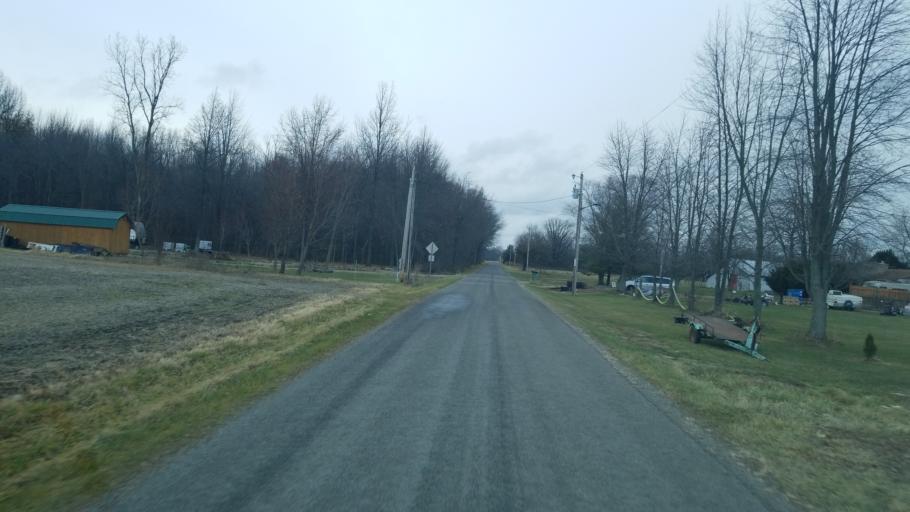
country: US
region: Ohio
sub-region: Union County
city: Richwood
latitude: 40.3286
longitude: -83.2496
